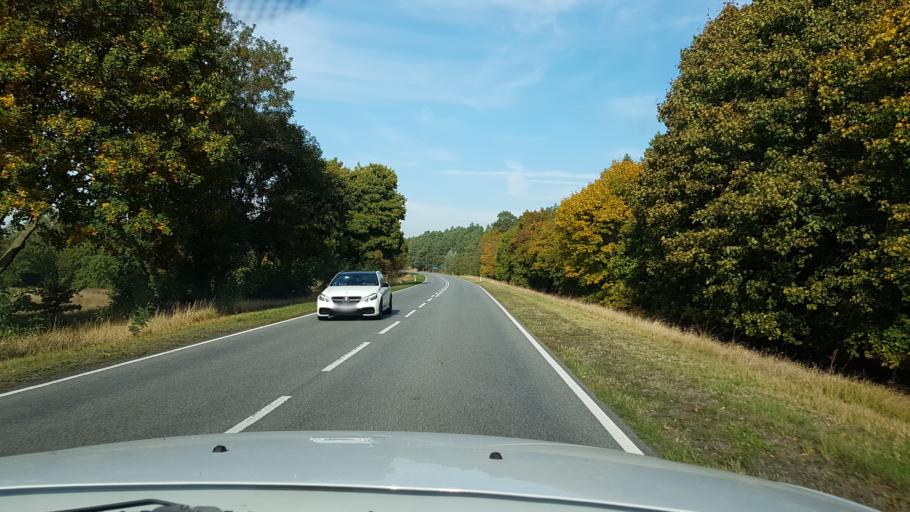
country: PL
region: West Pomeranian Voivodeship
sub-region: Powiat mysliborski
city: Nowogrodek Pomorski
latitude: 52.9151
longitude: 14.9687
